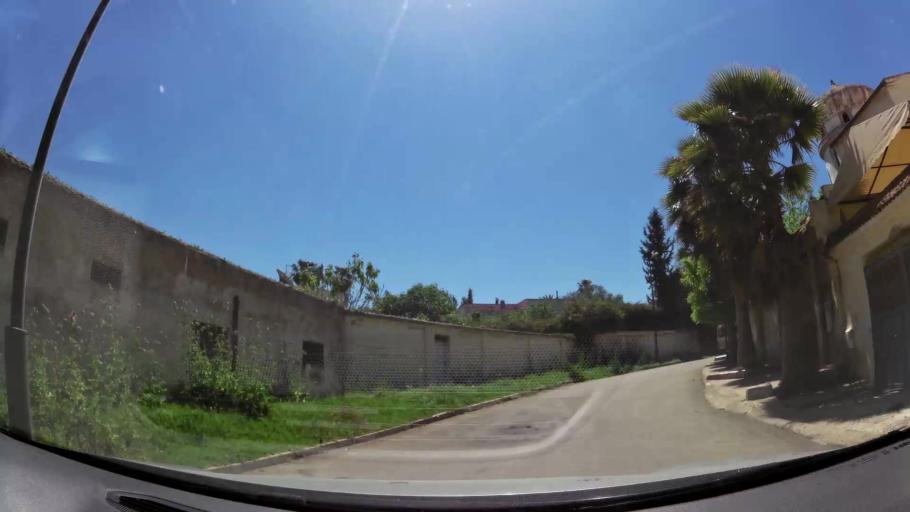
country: MA
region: Meknes-Tafilalet
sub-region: Meknes
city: Meknes
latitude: 33.8886
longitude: -5.5448
